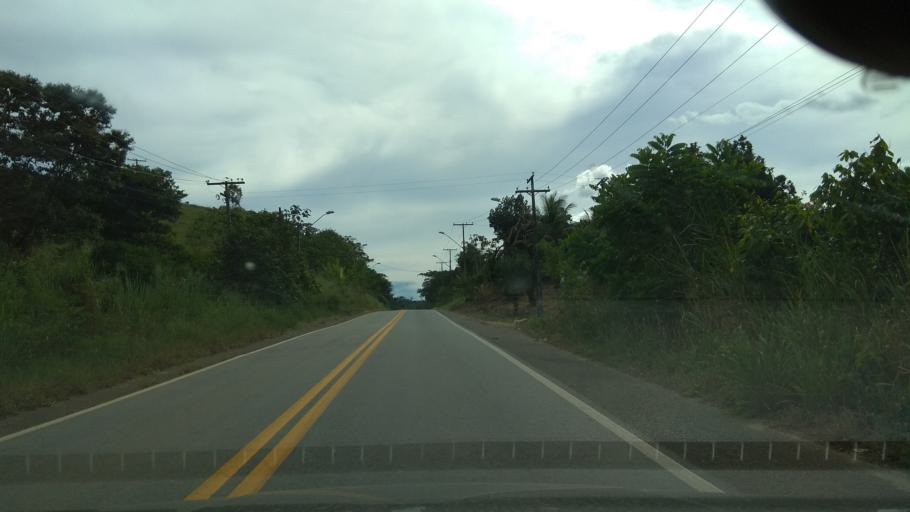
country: BR
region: Bahia
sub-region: Ubata
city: Ubata
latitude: -14.1966
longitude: -39.5426
